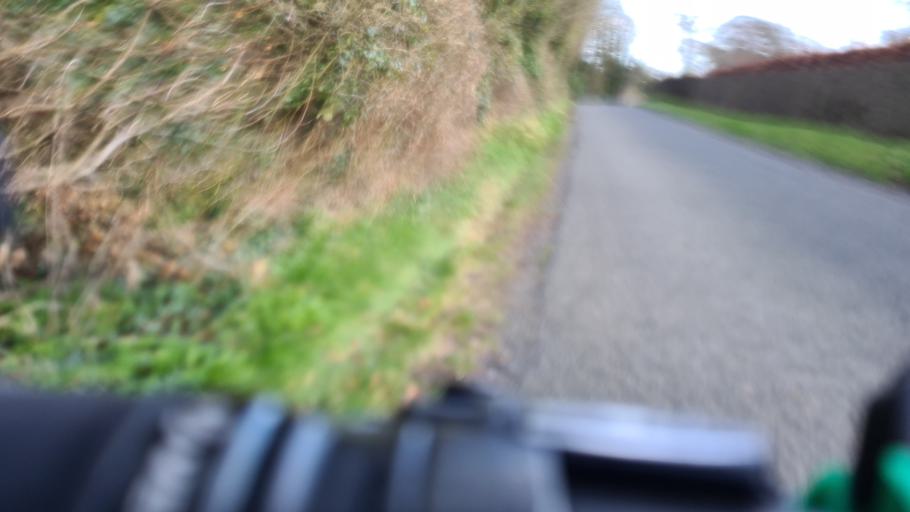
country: IE
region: Leinster
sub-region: Kildare
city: Celbridge
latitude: 53.3368
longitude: -6.5834
